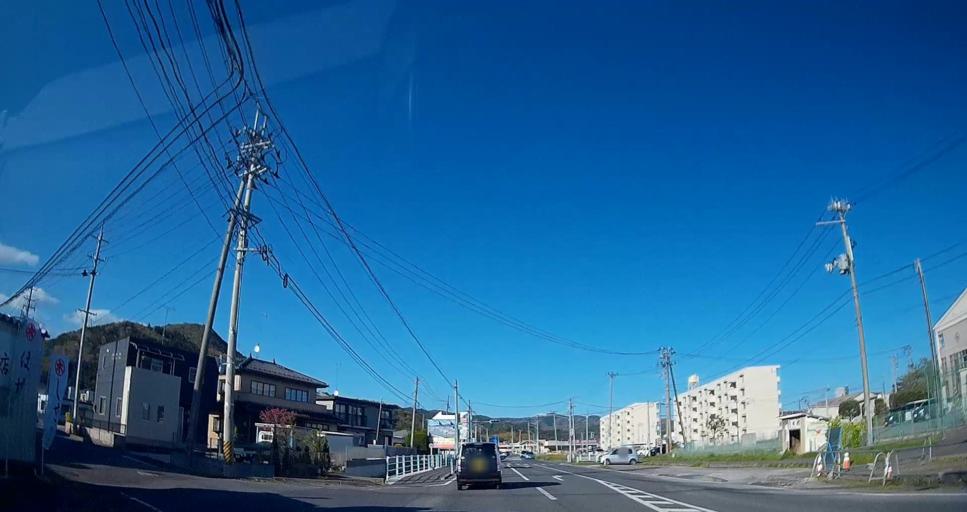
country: JP
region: Miyagi
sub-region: Oshika Gun
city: Onagawa Cho
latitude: 38.4259
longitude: 141.3714
